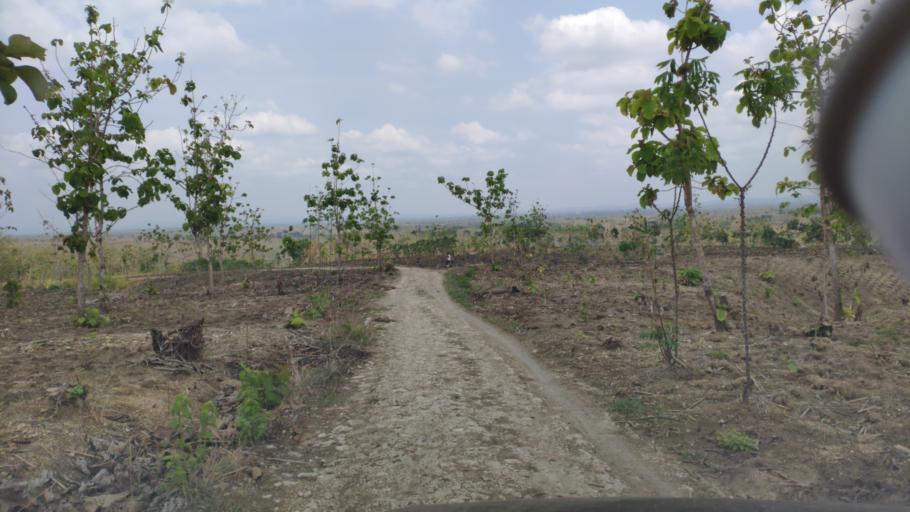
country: ID
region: Central Java
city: Gumiring
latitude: -7.0506
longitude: 111.3988
